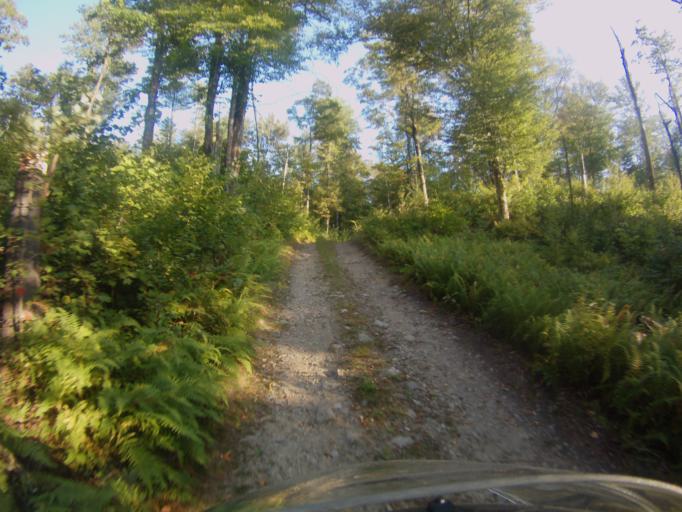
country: US
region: Vermont
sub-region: Addison County
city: Bristol
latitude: 44.0109
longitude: -73.0115
